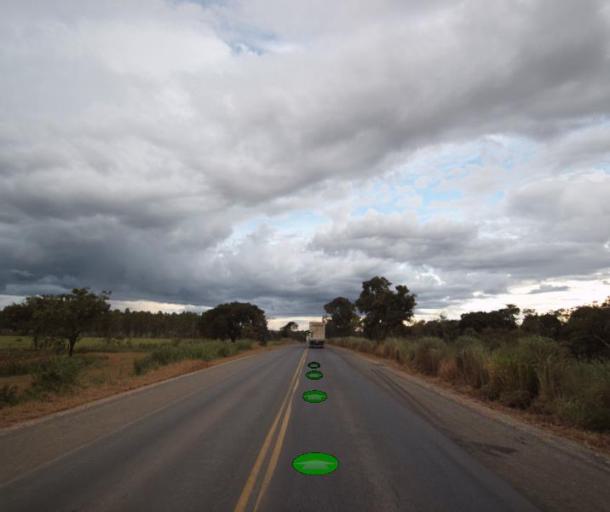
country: BR
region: Goias
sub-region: Uruacu
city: Uruacu
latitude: -14.7913
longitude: -49.2791
